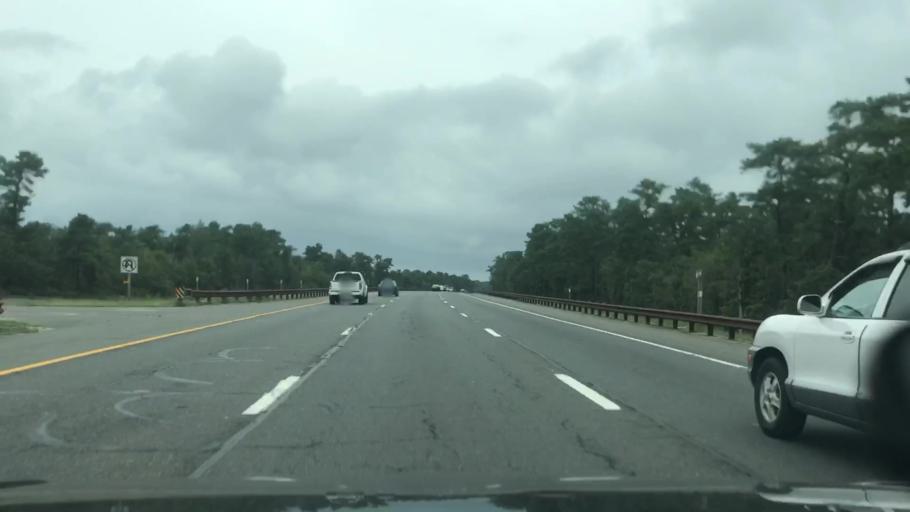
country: US
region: New Jersey
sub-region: Ocean County
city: Forked River
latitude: 39.8232
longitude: -74.2275
